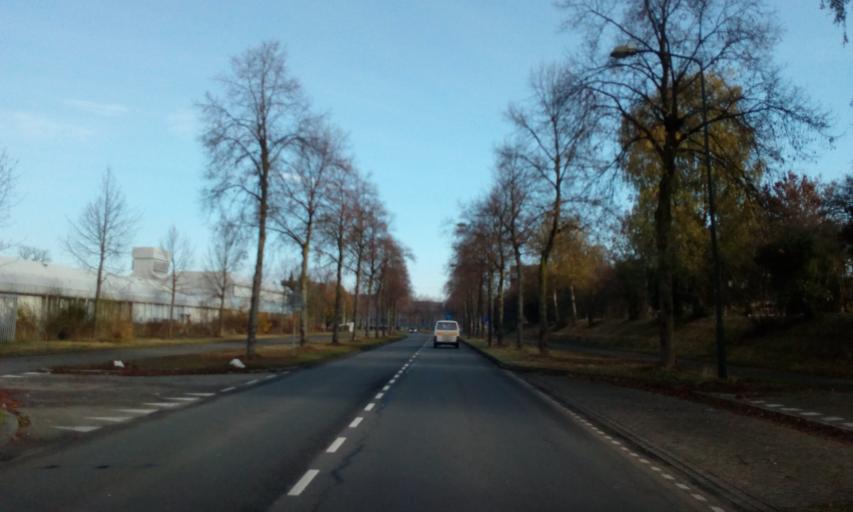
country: NL
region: Gelderland
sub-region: Gemeente Apeldoorn
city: Apeldoorn
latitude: 52.2037
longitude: 5.9535
